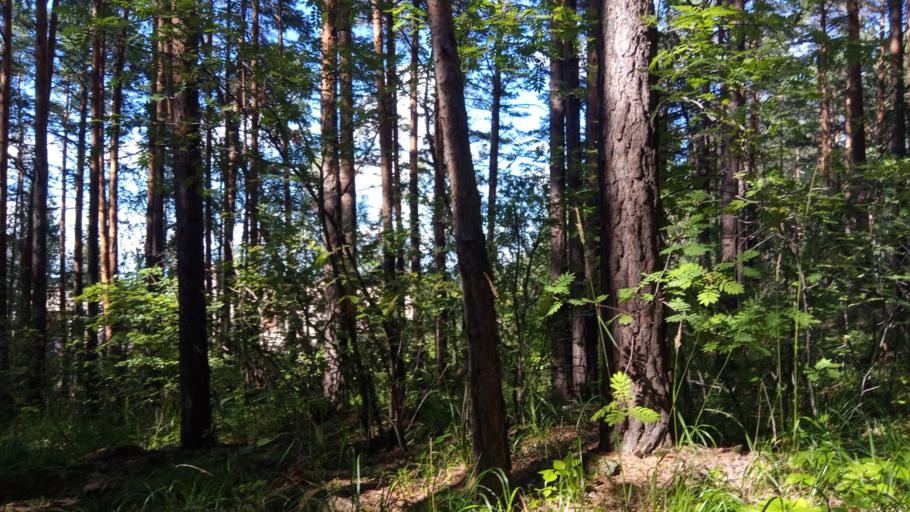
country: RU
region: Chelyabinsk
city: Chebarkul'
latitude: 55.0198
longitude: 60.3130
